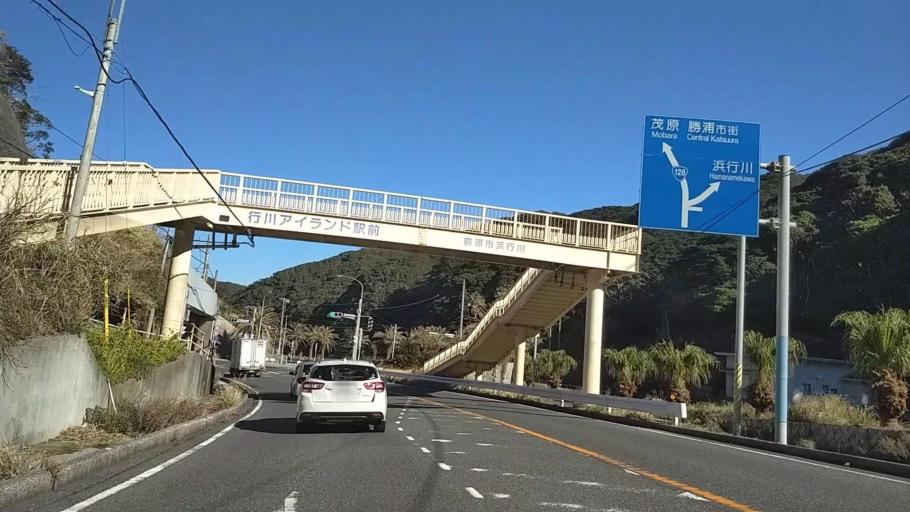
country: JP
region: Chiba
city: Katsuura
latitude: 35.1183
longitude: 140.2275
